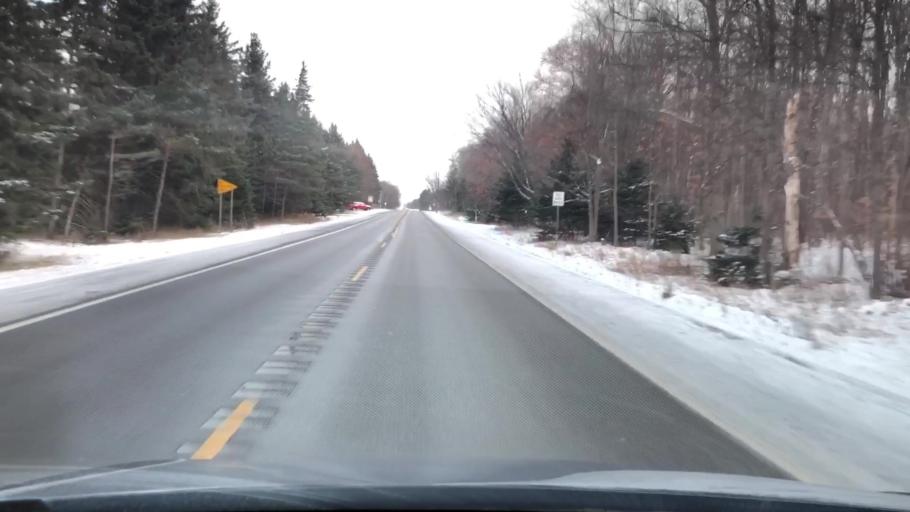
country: US
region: Michigan
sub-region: Grand Traverse County
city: Kingsley
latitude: 44.4655
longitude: -85.6975
